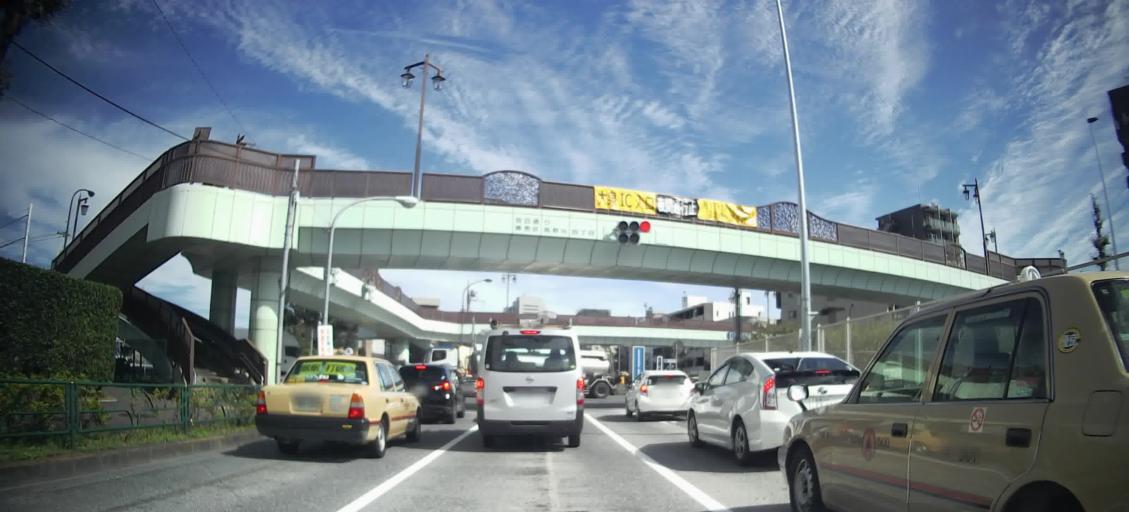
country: JP
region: Saitama
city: Wako
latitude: 35.7488
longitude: 139.6182
